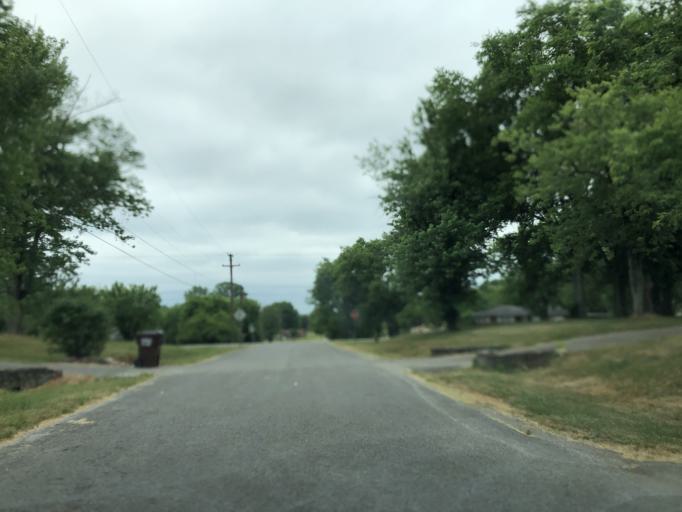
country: US
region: Tennessee
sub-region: Davidson County
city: Goodlettsville
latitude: 36.2807
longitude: -86.7588
